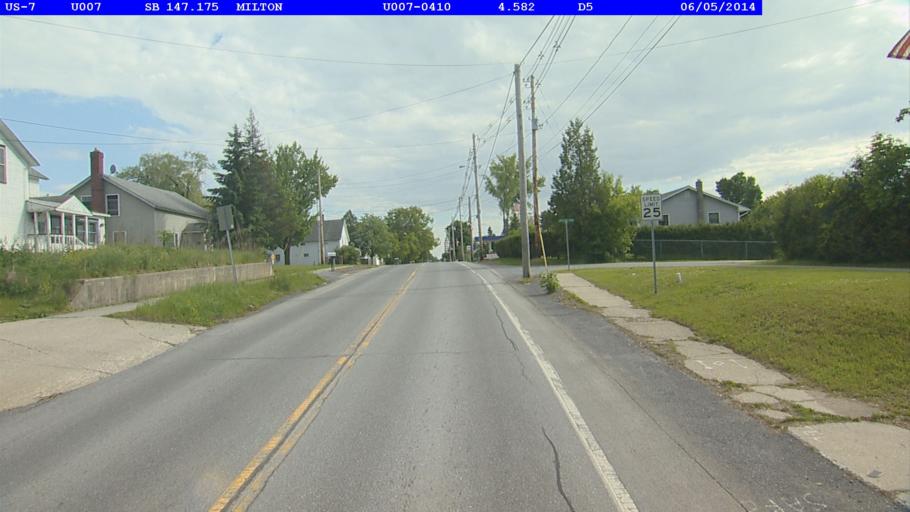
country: US
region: Vermont
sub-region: Chittenden County
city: Milton
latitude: 44.6334
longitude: -73.1147
